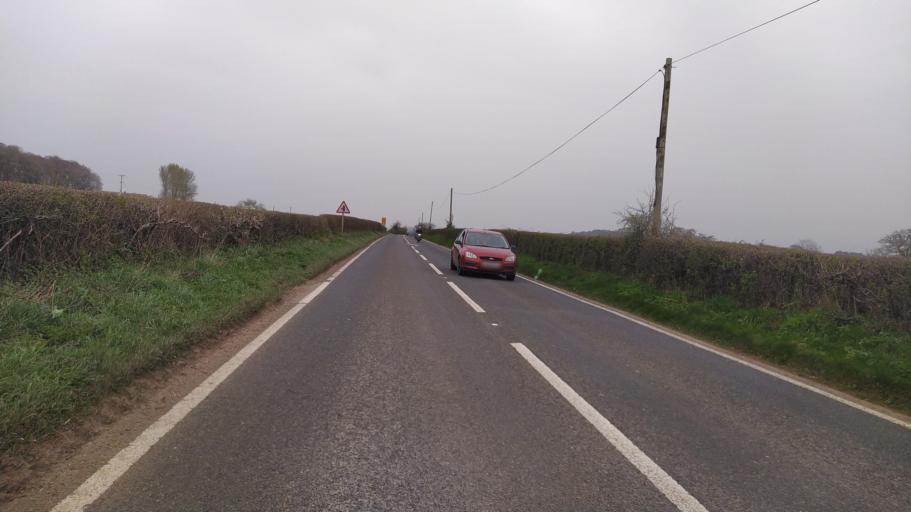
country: GB
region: England
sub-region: Somerset
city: Chard
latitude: 50.8984
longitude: -2.9489
